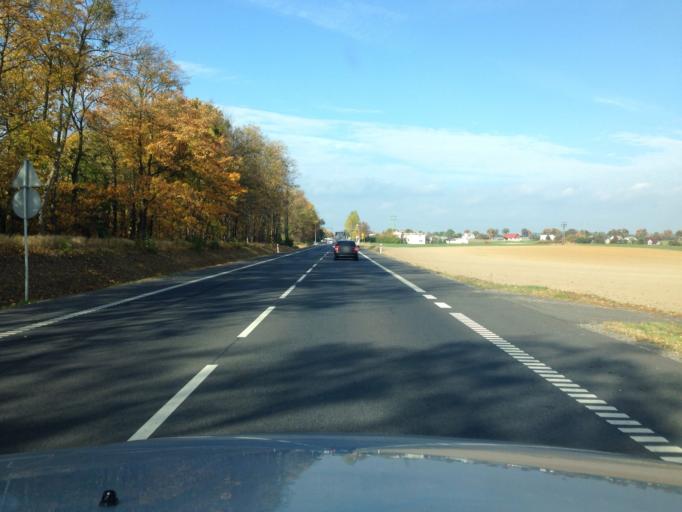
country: PL
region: Kujawsko-Pomorskie
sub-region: Powiat swiecki
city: Warlubie
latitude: 53.5760
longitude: 18.6411
